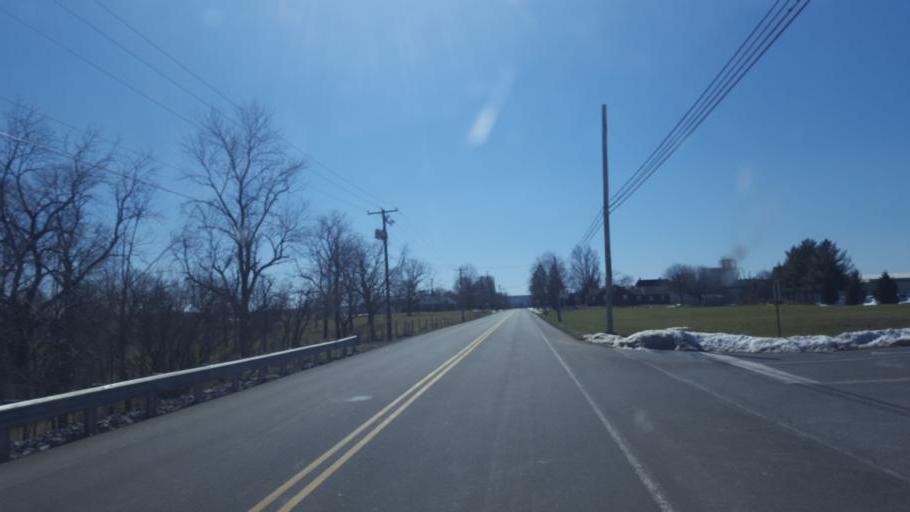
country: US
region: Pennsylvania
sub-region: Lancaster County
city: Blue Ball
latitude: 40.1391
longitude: -76.0296
